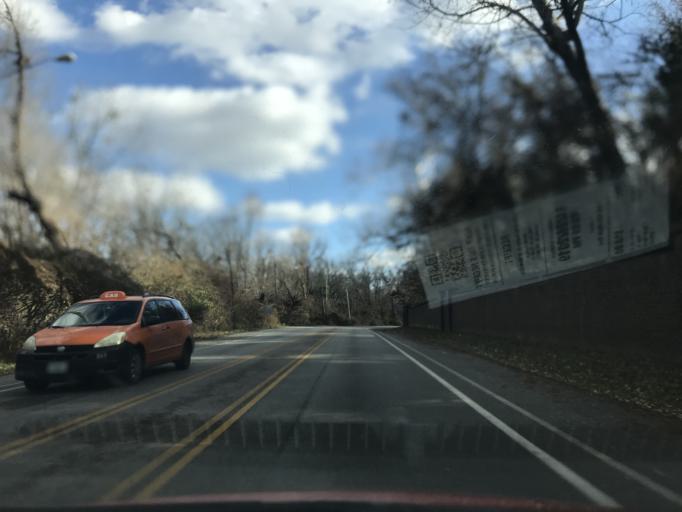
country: US
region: Indiana
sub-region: Clark County
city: Jeffersonville
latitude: 38.2494
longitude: -85.7134
